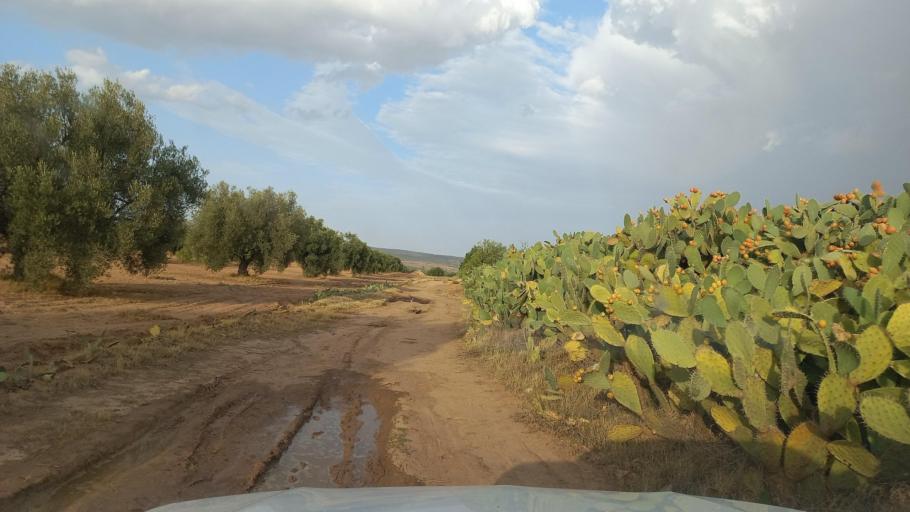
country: TN
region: Al Qasrayn
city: Sbiba
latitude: 35.2855
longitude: 9.0728
